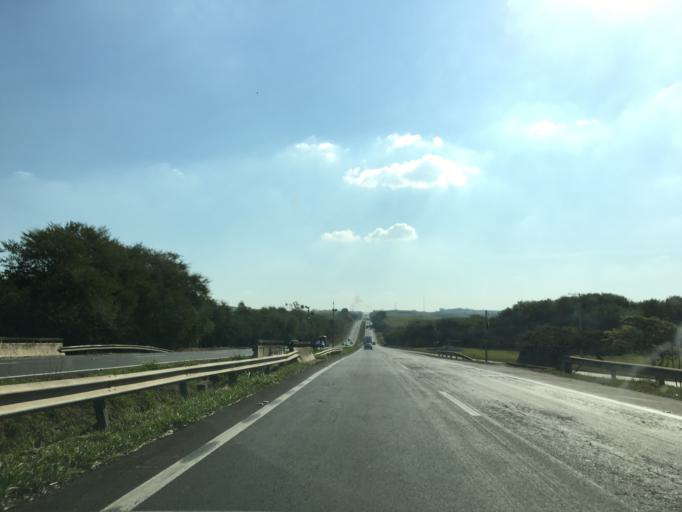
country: BR
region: Sao Paulo
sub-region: Santa Barbara D'Oeste
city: Santa Barbara d'Oeste
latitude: -22.7564
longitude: -47.4758
